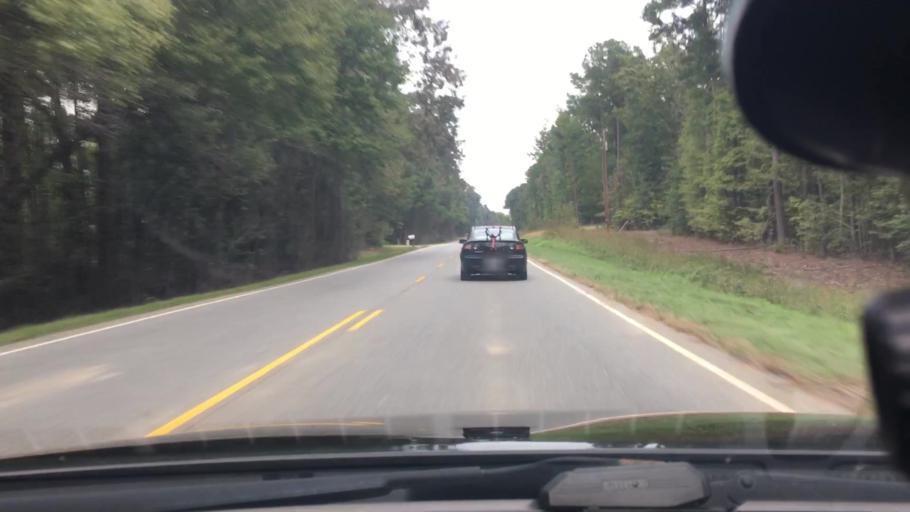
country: US
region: North Carolina
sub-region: Moore County
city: Robbins
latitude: 35.3844
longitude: -79.6554
